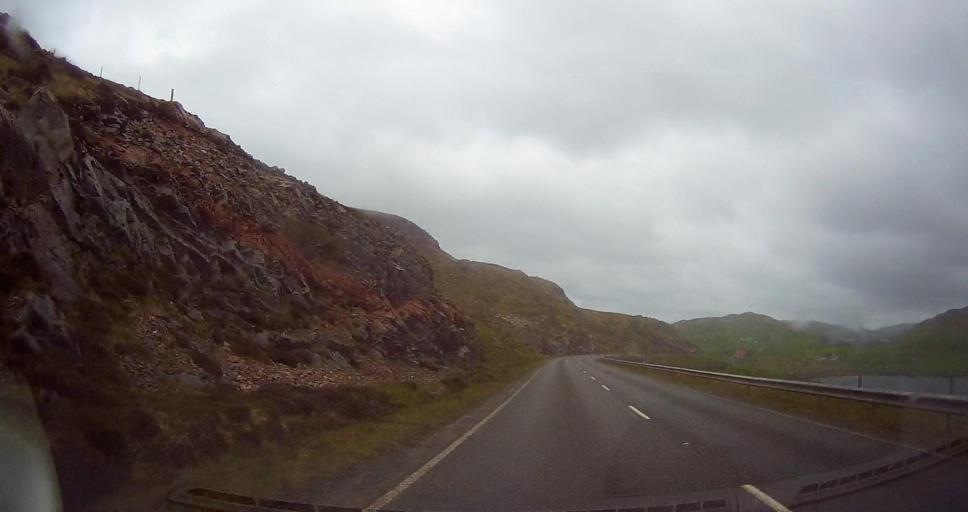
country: GB
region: Scotland
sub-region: Shetland Islands
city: Lerwick
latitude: 60.4127
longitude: -1.3915
